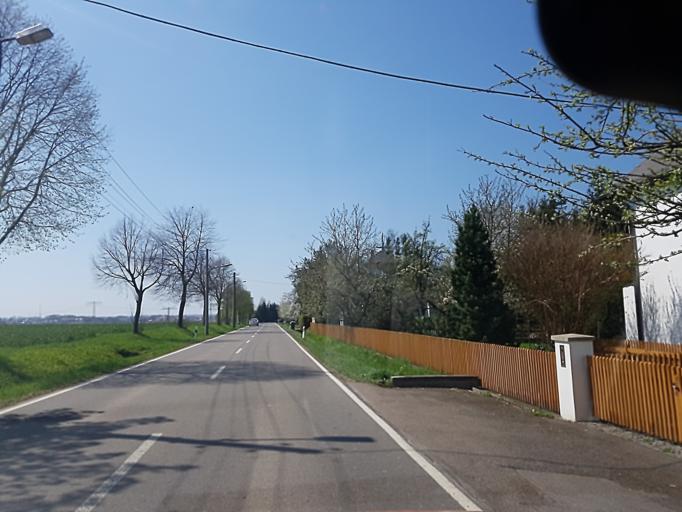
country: DE
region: Saxony
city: Leisnig
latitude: 51.1715
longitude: 12.9516
